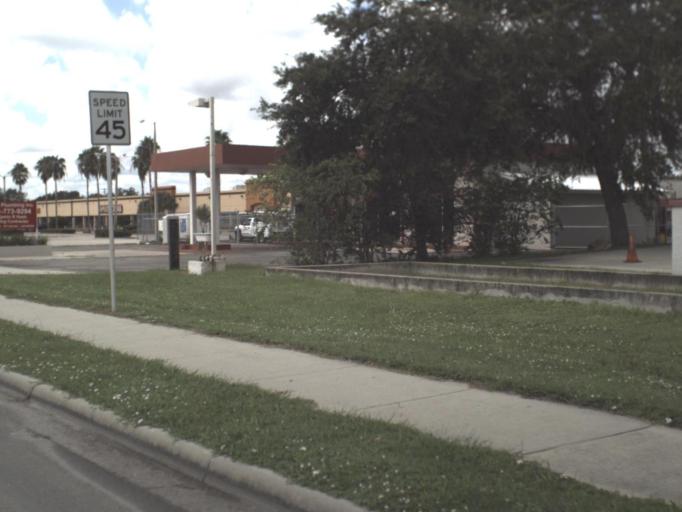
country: US
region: Florida
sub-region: Hardee County
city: Wauchula
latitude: 27.5357
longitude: -81.8095
